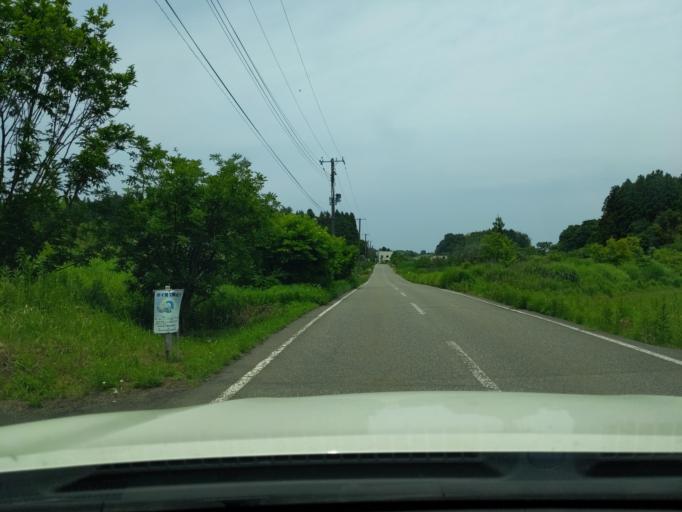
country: JP
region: Niigata
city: Kashiwazaki
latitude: 37.3417
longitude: 138.5531
